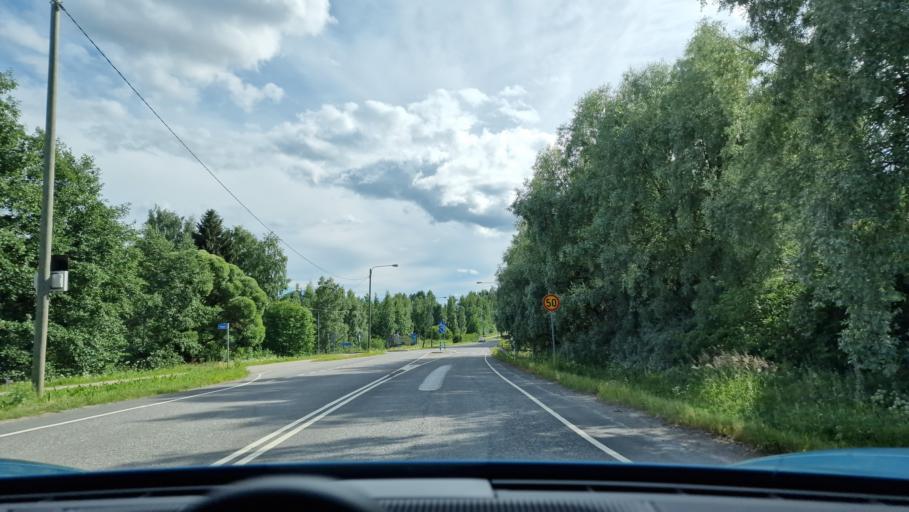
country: FI
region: Pirkanmaa
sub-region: Tampere
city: Orivesi
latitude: 61.6490
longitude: 24.3580
